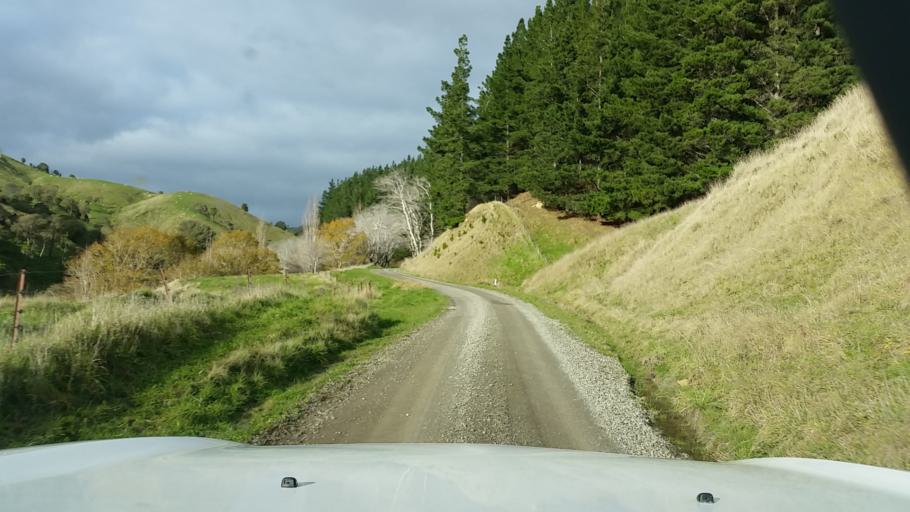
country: NZ
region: Wellington
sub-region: Masterton District
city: Masterton
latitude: -41.0384
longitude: 175.7161
